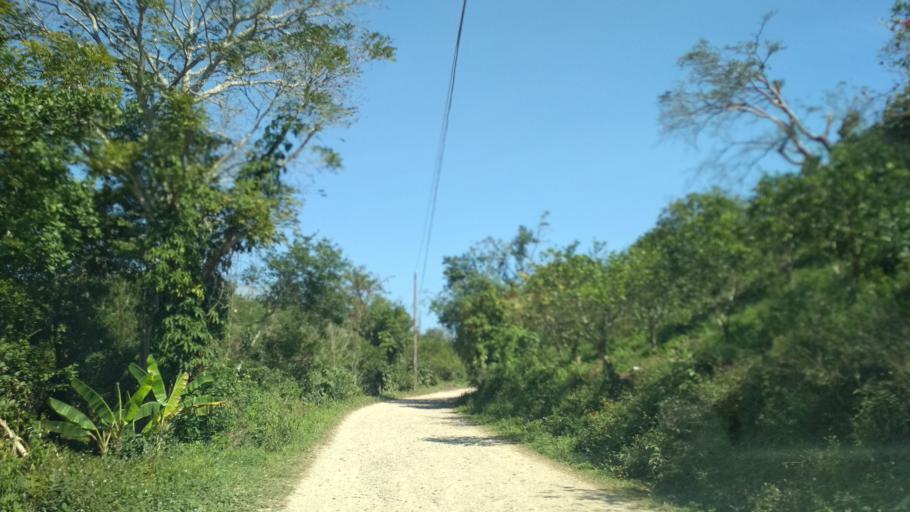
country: MX
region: Veracruz
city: Gutierrez Zamora
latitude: 20.4690
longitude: -97.1542
